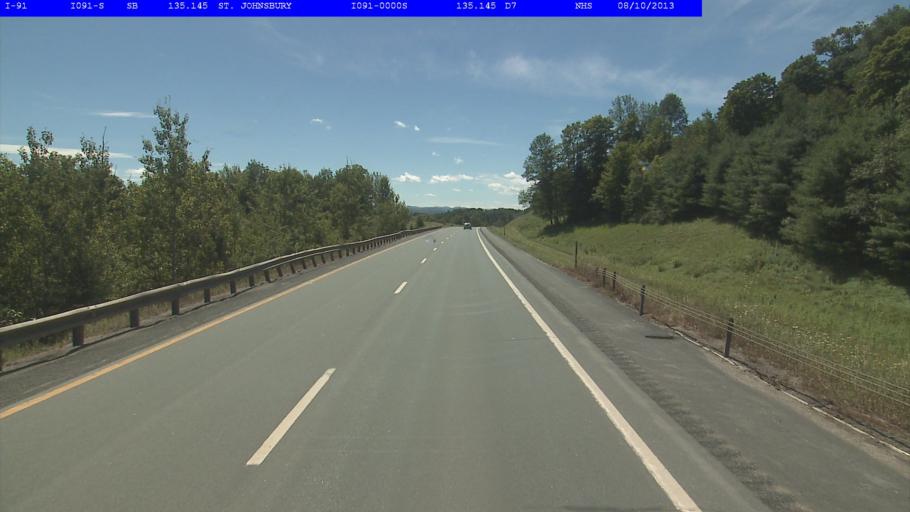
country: US
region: Vermont
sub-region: Caledonia County
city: Lyndon
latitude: 44.4915
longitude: -72.0223
